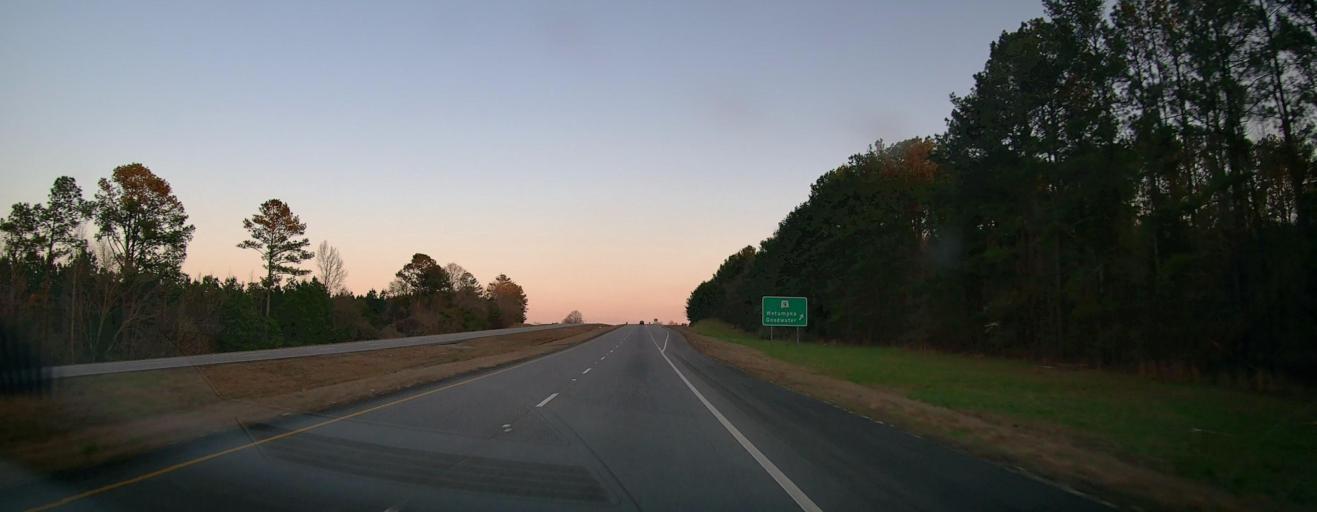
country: US
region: Alabama
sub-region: Coosa County
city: Goodwater
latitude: 32.9905
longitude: -86.0714
